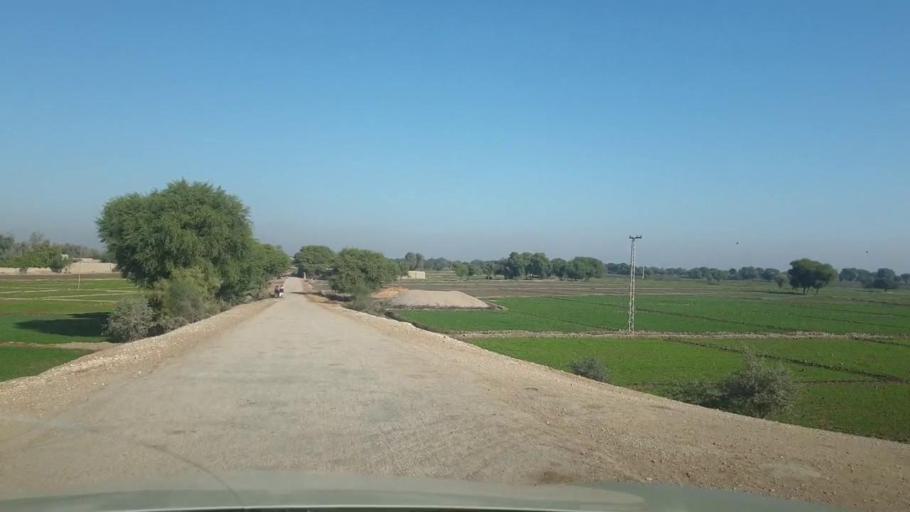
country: PK
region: Sindh
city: Bhan
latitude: 26.5592
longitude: 67.6640
